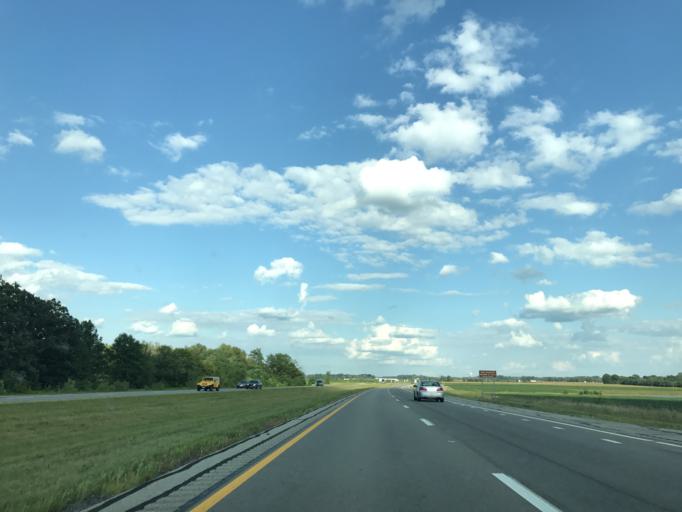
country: US
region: Ohio
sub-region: Crawford County
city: Galion
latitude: 40.7627
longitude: -82.8492
